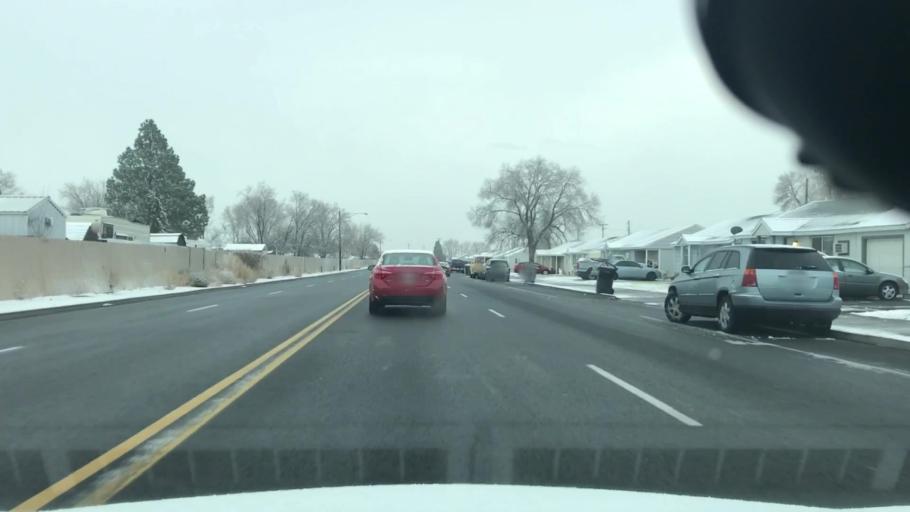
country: US
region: Washington
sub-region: Grant County
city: Moses Lake North
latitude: 47.1776
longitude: -119.3219
